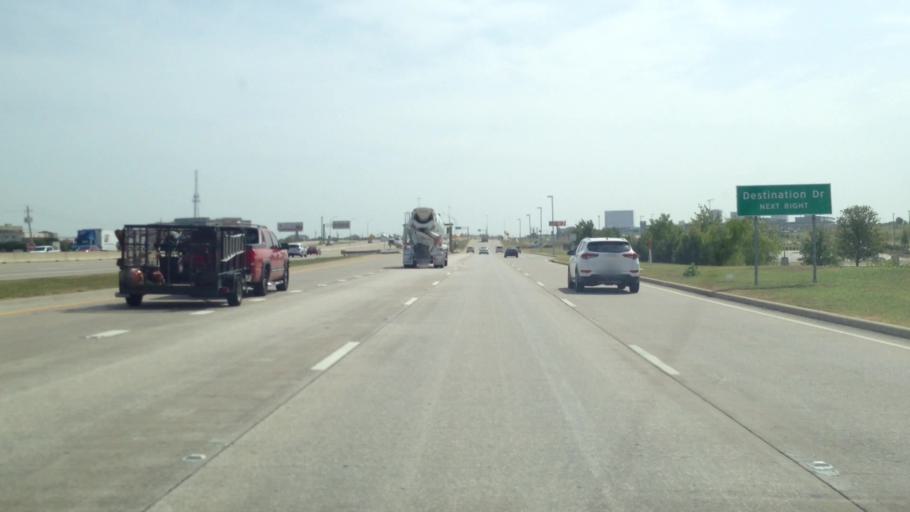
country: US
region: Texas
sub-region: Denton County
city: The Colony
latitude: 33.0784
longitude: -96.8605
